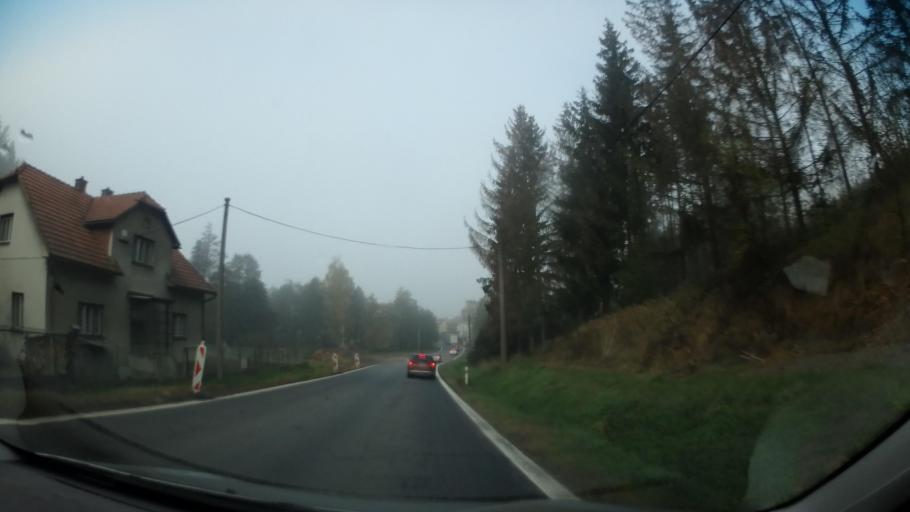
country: CZ
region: Vysocina
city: Krizanov
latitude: 49.4705
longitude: 16.1269
